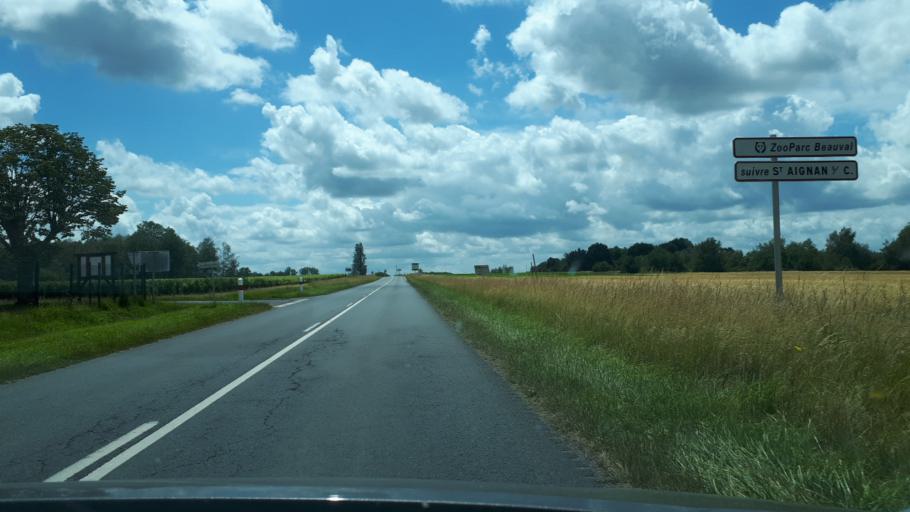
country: FR
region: Centre
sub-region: Departement du Loir-et-Cher
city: Contres
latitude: 47.3984
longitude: 1.4119
